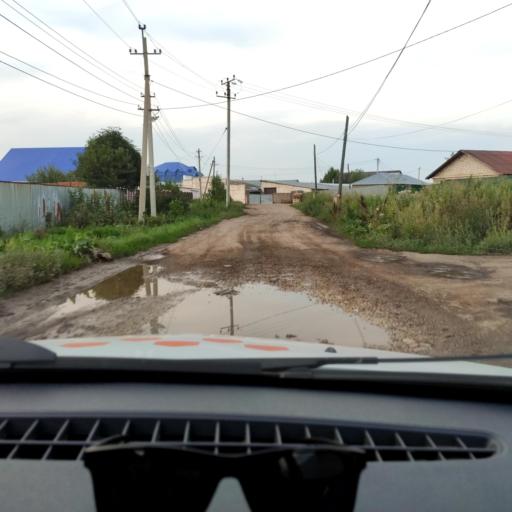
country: RU
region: Bashkortostan
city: Ufa
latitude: 54.6125
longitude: 55.9321
